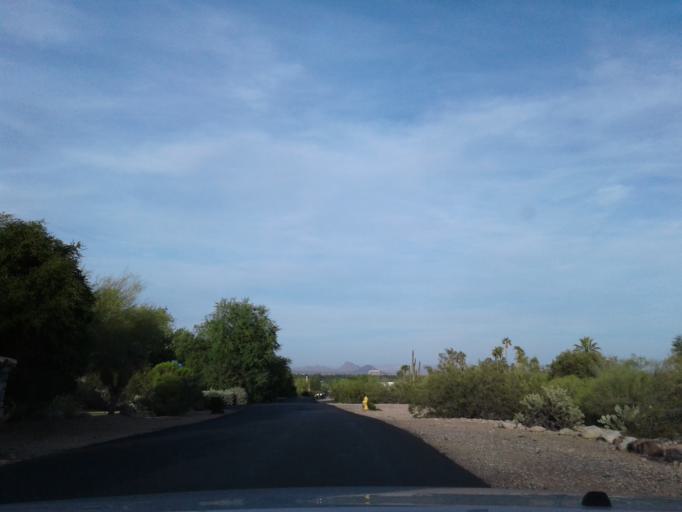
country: US
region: Arizona
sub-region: Maricopa County
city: Paradise Valley
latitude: 33.5457
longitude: -111.9462
